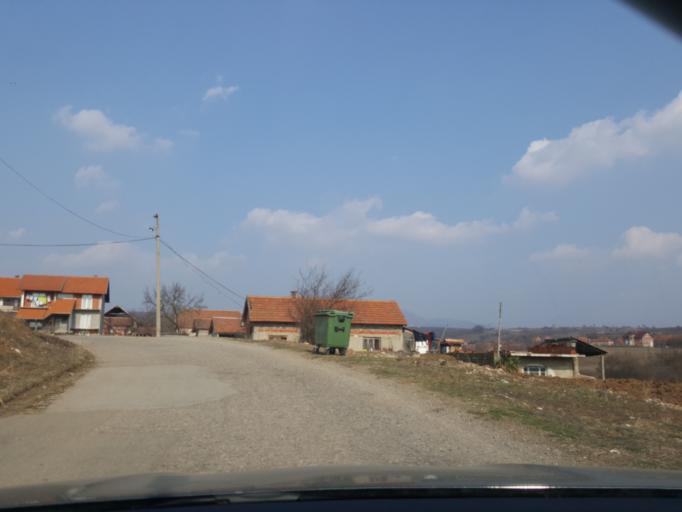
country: RS
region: Central Serbia
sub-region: Nisavski Okrug
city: Aleksinac
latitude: 43.5249
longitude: 21.7347
